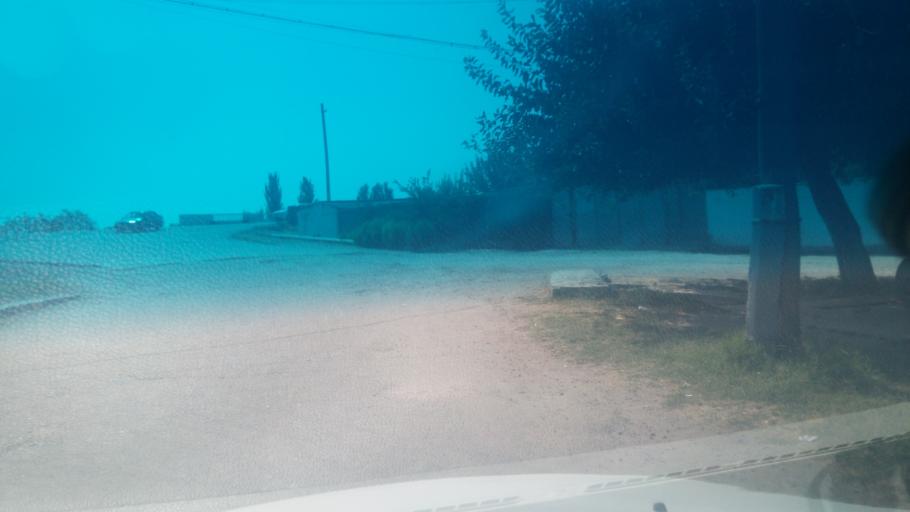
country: UZ
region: Sirdaryo
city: Sirdaryo
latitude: 40.8198
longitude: 68.6696
